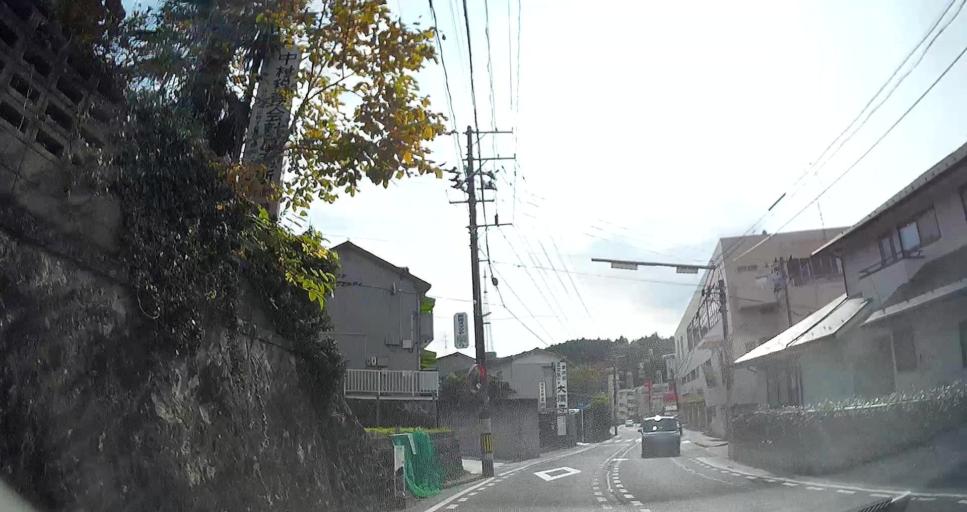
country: JP
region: Miyagi
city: Sendai
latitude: 38.2450
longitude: 140.8724
